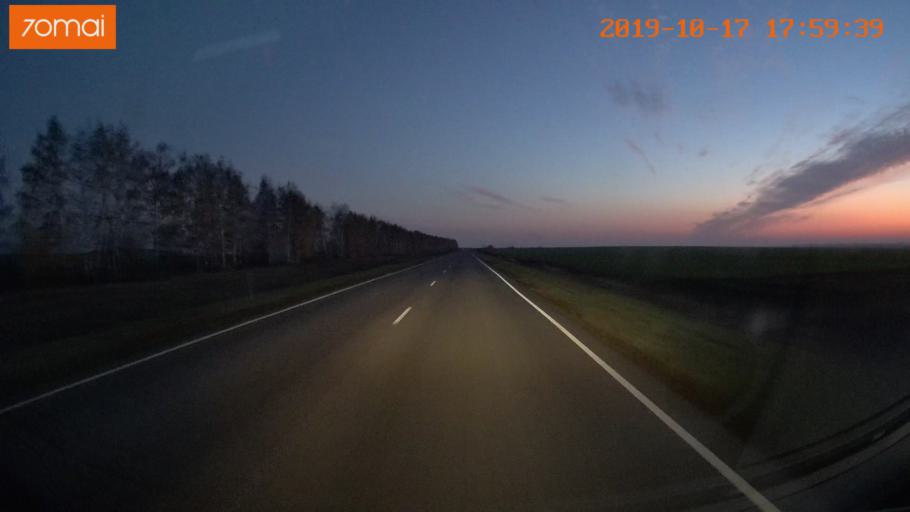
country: RU
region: Tula
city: Kurkino
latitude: 53.5344
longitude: 38.6203
